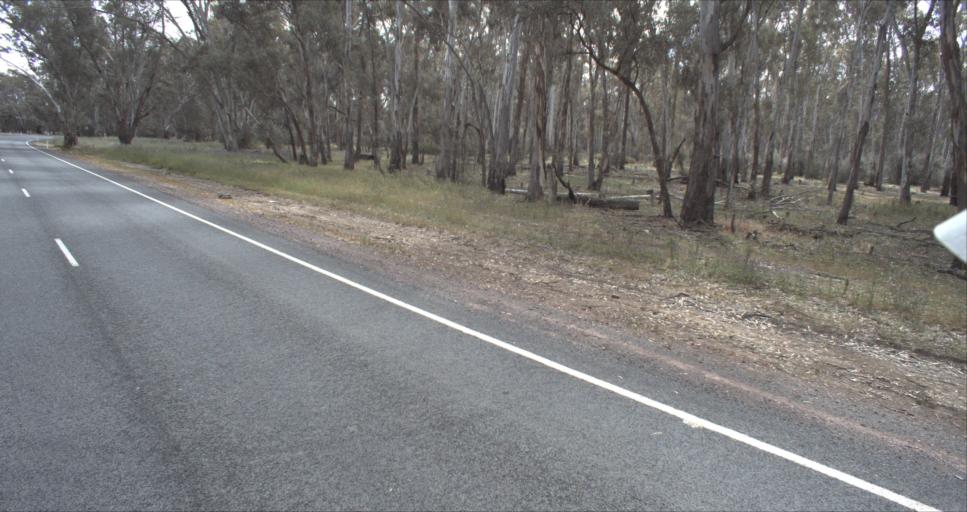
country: AU
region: New South Wales
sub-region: Leeton
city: Leeton
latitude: -34.6406
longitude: 146.3698
